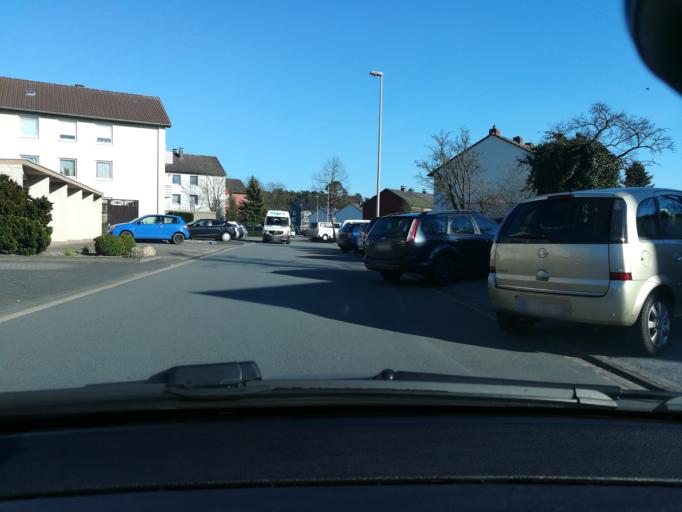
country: DE
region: North Rhine-Westphalia
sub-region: Regierungsbezirk Detmold
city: Oerlinghausen
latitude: 51.9518
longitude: 8.5966
